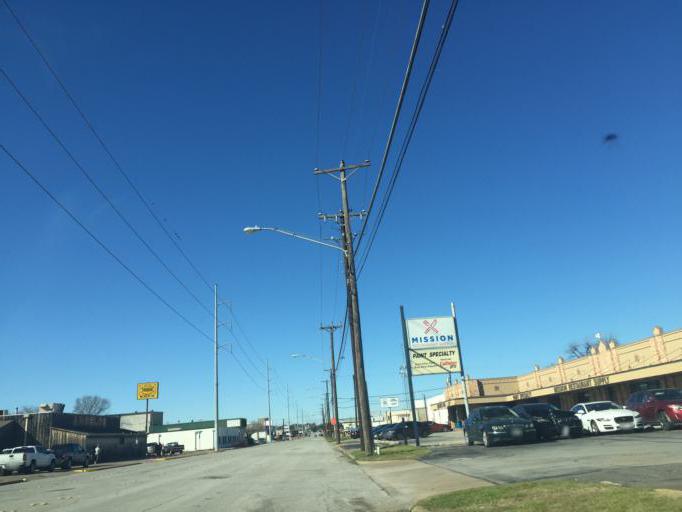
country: US
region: Texas
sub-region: Tarrant County
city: Fort Worth
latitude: 32.7592
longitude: -97.3516
